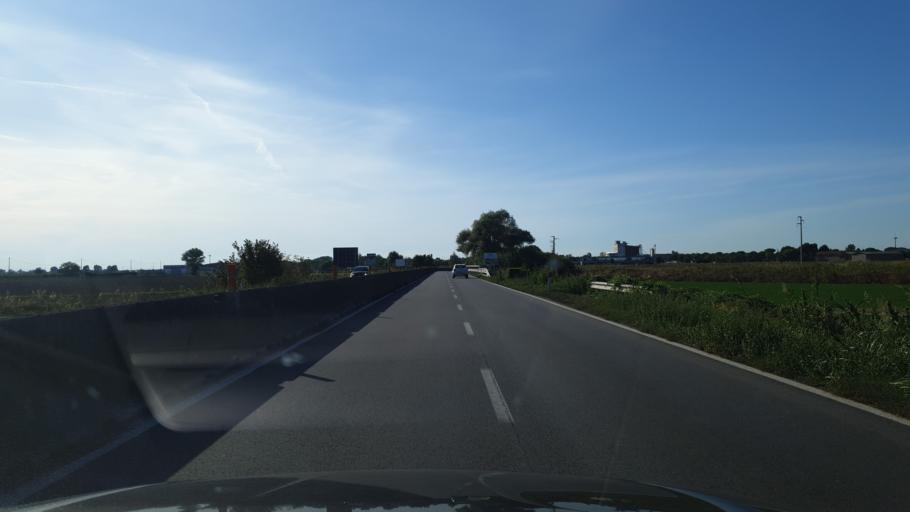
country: IT
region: Emilia-Romagna
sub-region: Provincia di Ravenna
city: Classe
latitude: 44.3763
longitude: 12.2211
